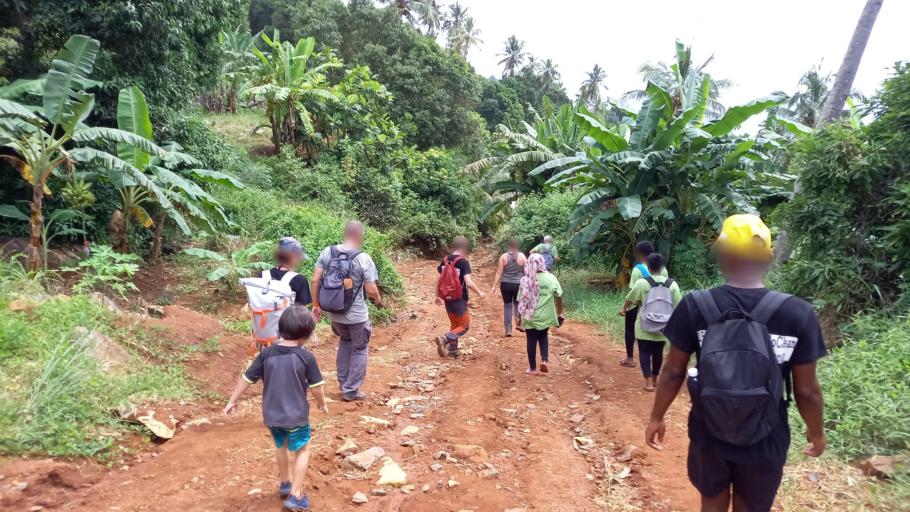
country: YT
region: Acoua
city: Acoua
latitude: -12.7118
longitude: 45.0548
